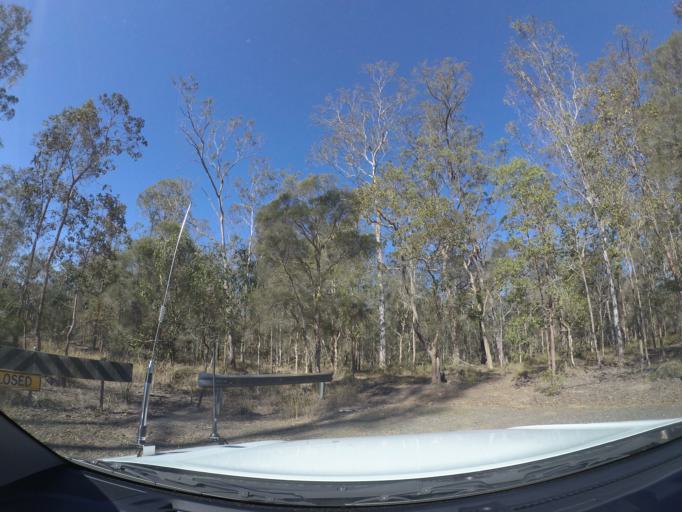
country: AU
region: Queensland
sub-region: Logan
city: Park Ridge South
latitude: -27.7451
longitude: 153.0509
